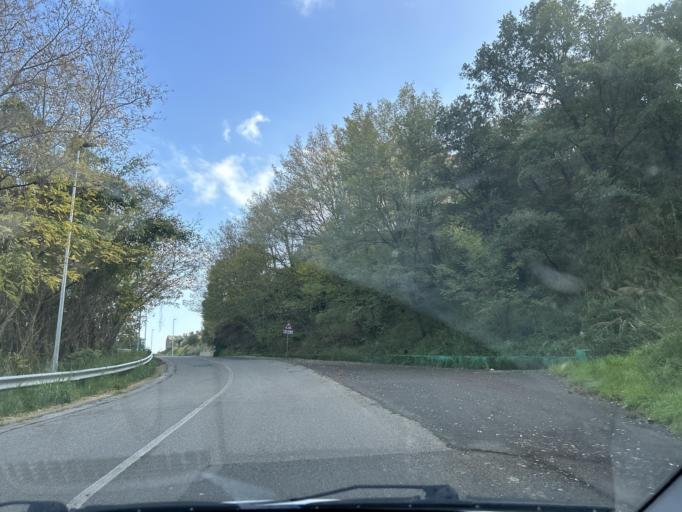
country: IT
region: Calabria
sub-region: Provincia di Catanzaro
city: Montepaone
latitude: 38.7216
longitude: 16.5027
